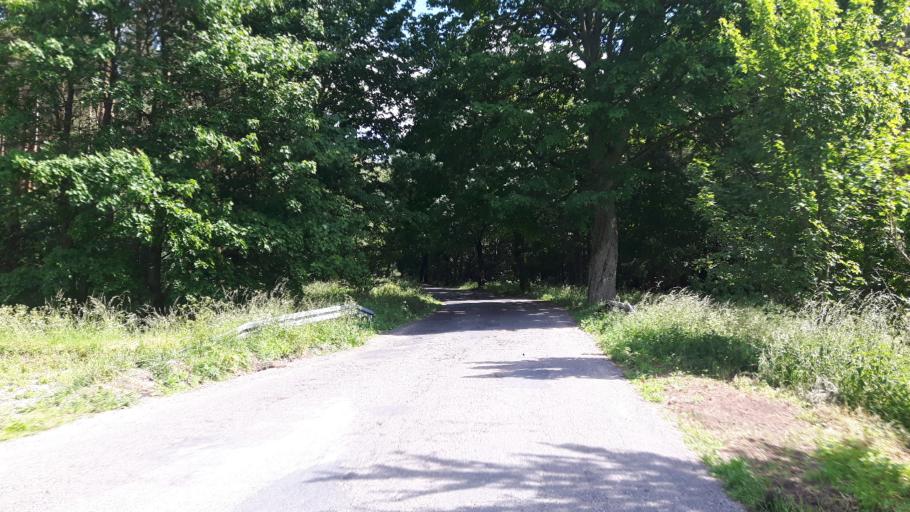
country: PL
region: West Pomeranian Voivodeship
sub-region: Powiat goleniowski
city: Osina
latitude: 53.6771
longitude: 15.0155
